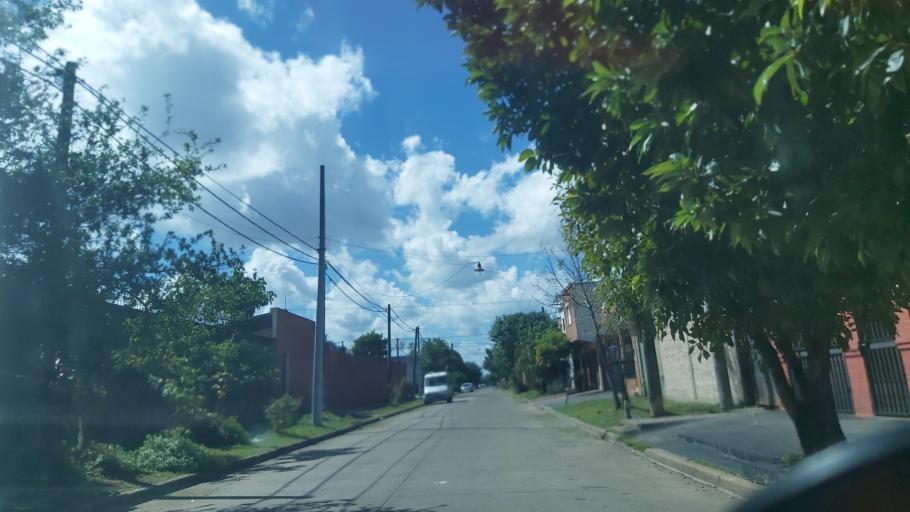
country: AR
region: Corrientes
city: Corrientes
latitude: -27.4791
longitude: -58.8484
